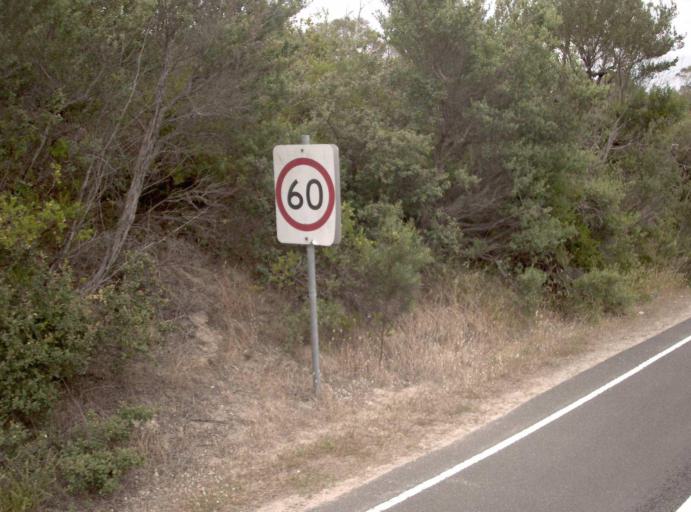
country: AU
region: Victoria
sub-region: Mornington Peninsula
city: Blairgowrie
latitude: -38.3535
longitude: 144.7624
